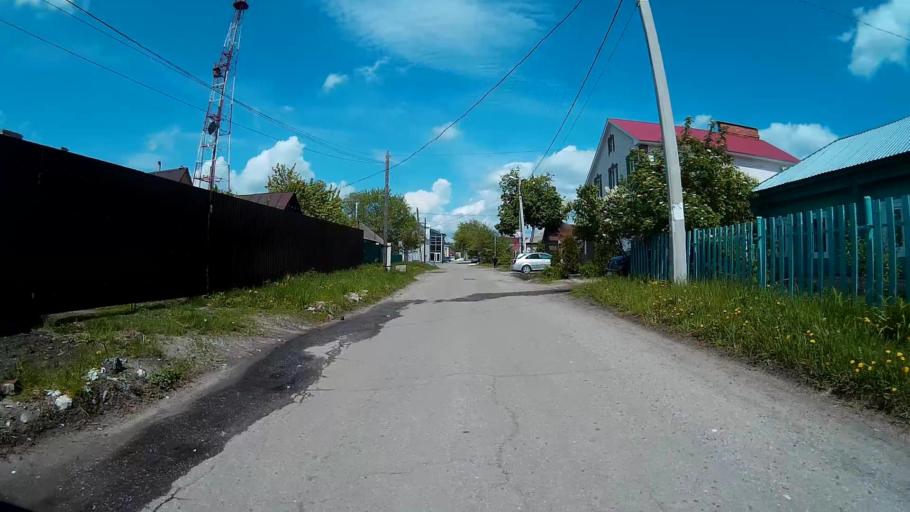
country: RU
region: Ulyanovsk
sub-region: Ulyanovskiy Rayon
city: Ulyanovsk
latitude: 54.3403
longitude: 48.3832
